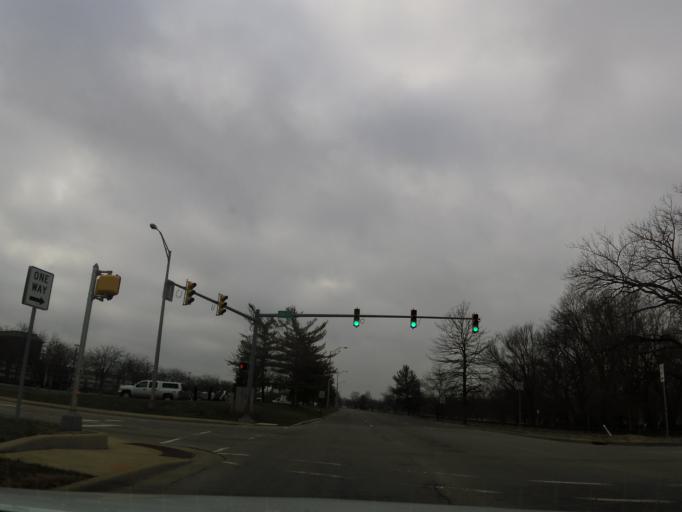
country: US
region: Indiana
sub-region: Bartholomew County
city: Columbus
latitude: 39.2069
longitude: -85.9250
